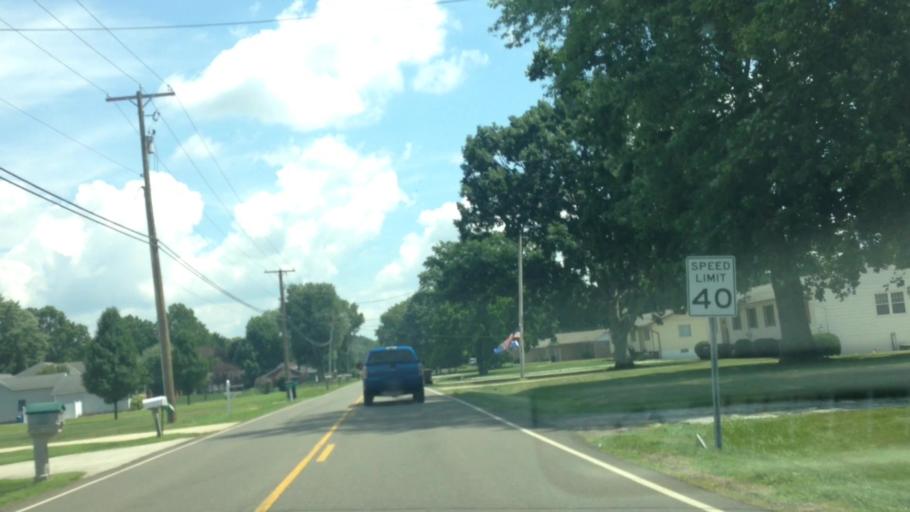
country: US
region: Ohio
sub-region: Summit County
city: New Franklin
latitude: 40.9493
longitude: -81.5390
